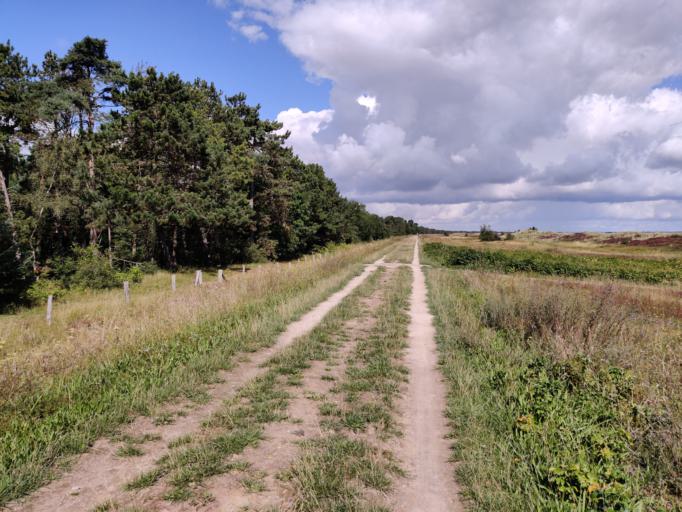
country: DK
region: Zealand
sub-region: Guldborgsund Kommune
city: Nykobing Falster
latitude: 54.6465
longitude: 11.9599
